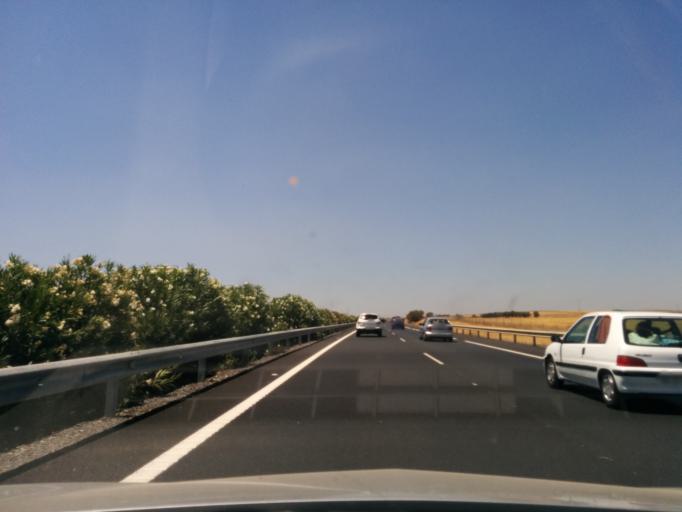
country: ES
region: Andalusia
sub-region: Provincia de Huelva
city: San Juan del Puerto
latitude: 37.3307
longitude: -6.8113
